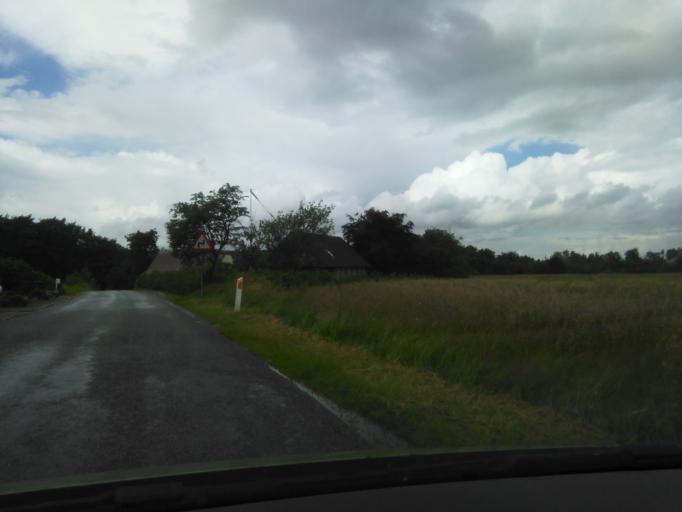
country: DK
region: Central Jutland
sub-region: Horsens Kommune
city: Braedstrup
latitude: 55.9733
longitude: 9.6993
